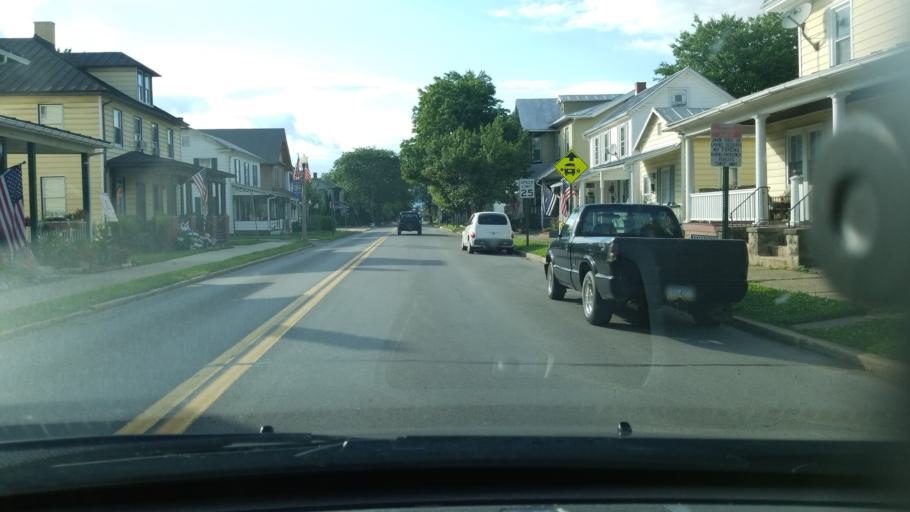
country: US
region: Pennsylvania
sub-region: Northumberland County
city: Watsontown
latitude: 41.0880
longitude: -76.8671
